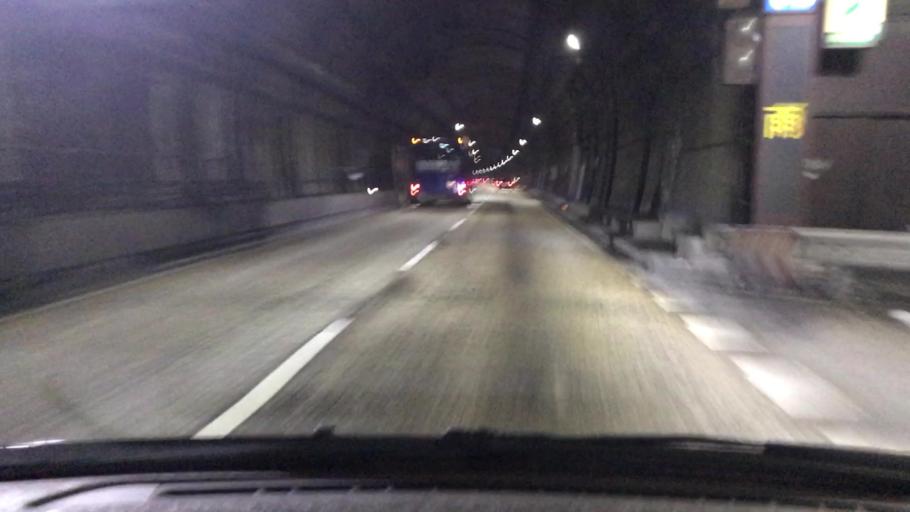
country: JP
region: Hyogo
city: Kobe
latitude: 34.7118
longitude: 135.1917
